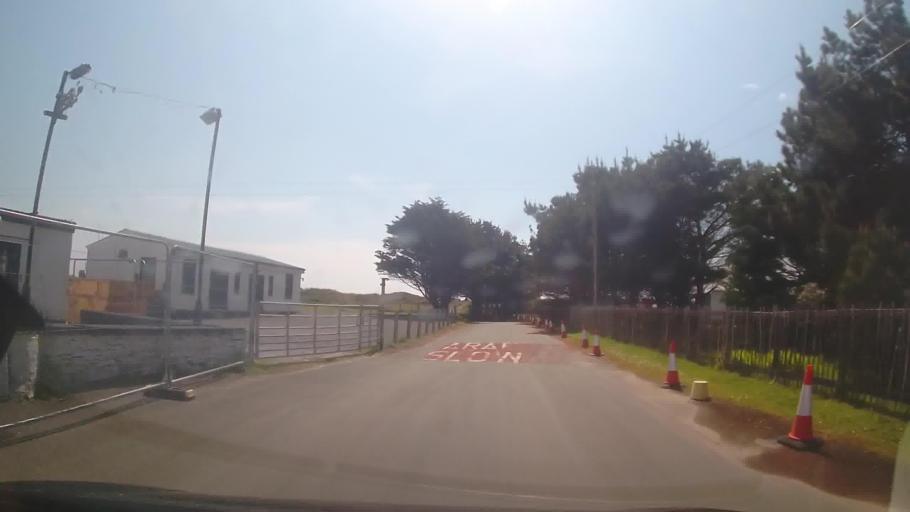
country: GB
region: Wales
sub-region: Gwynedd
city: Criccieth
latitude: 52.9151
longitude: -4.1909
